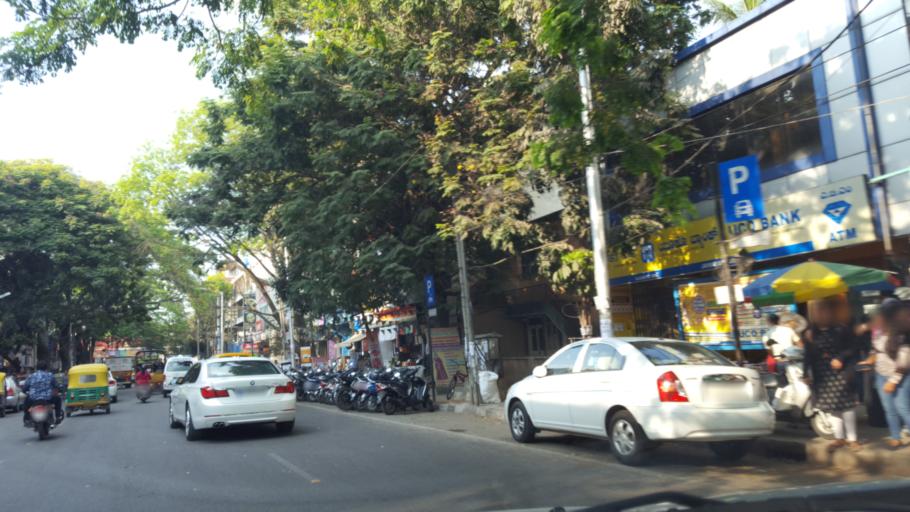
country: IN
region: Karnataka
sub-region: Bangalore Urban
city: Bangalore
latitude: 12.9314
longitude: 77.5839
